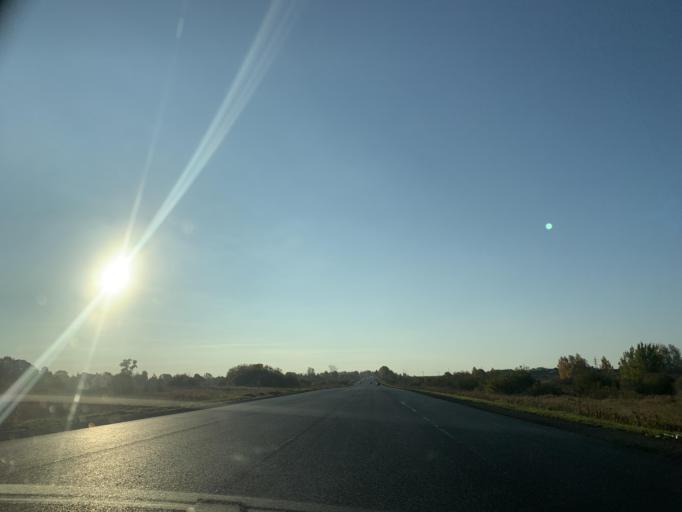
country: RU
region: Jaroslavl
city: Konstantinovskiy
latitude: 57.7962
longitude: 39.6005
